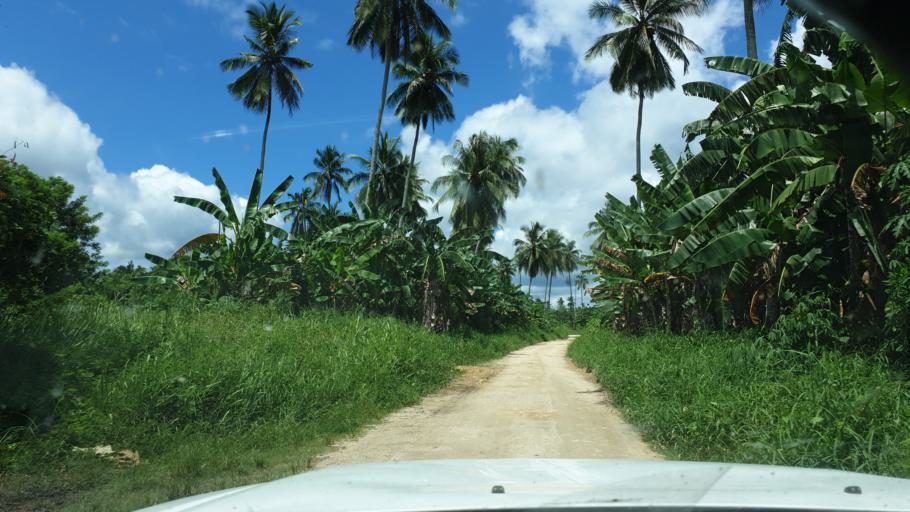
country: PG
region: East Sepik
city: Angoram
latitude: -4.2021
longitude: 144.8900
